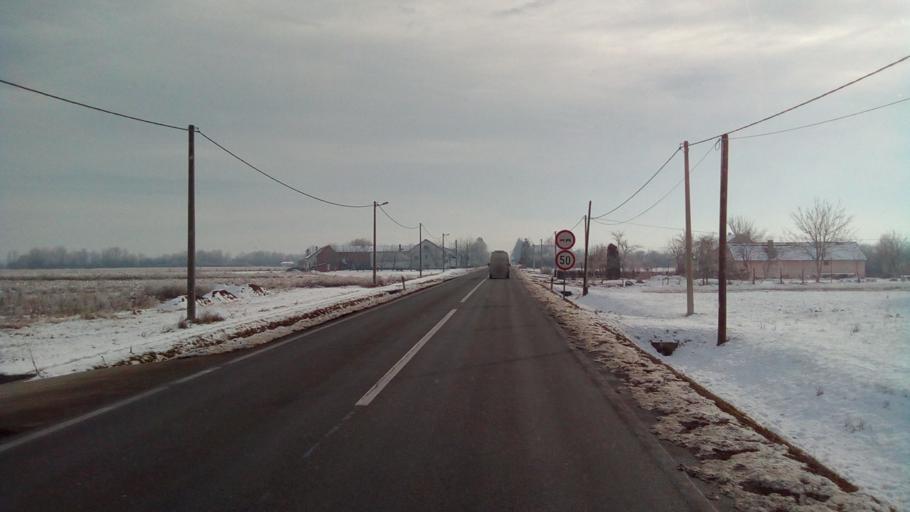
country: HR
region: Sisacko-Moslavacka
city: Lekenik
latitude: 45.5471
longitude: 16.2342
